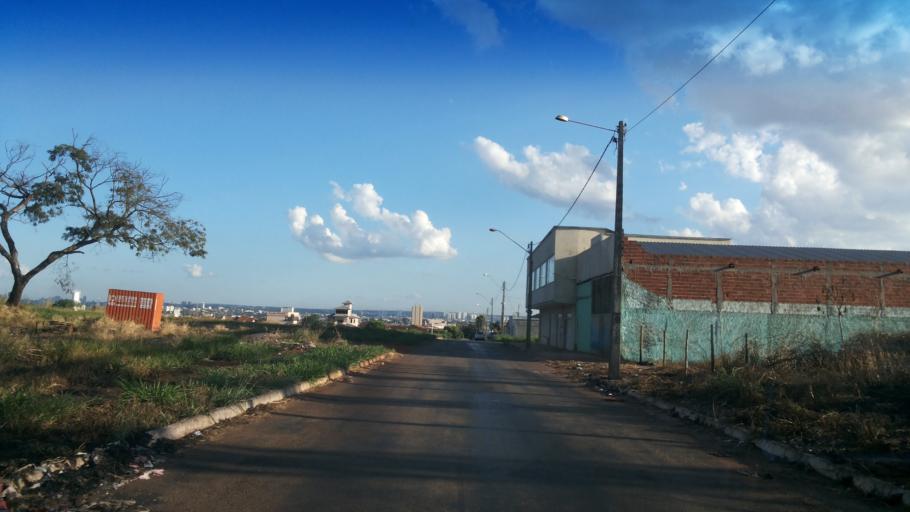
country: BR
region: Goias
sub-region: Goiania
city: Goiania
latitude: -16.6434
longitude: -49.2991
